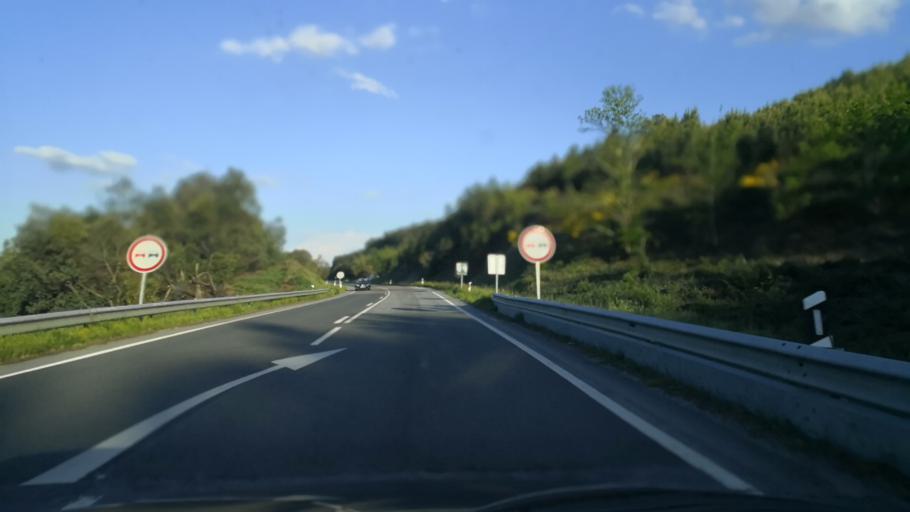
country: PT
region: Portalegre
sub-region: Marvao
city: Marvao
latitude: 39.3760
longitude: -7.3628
